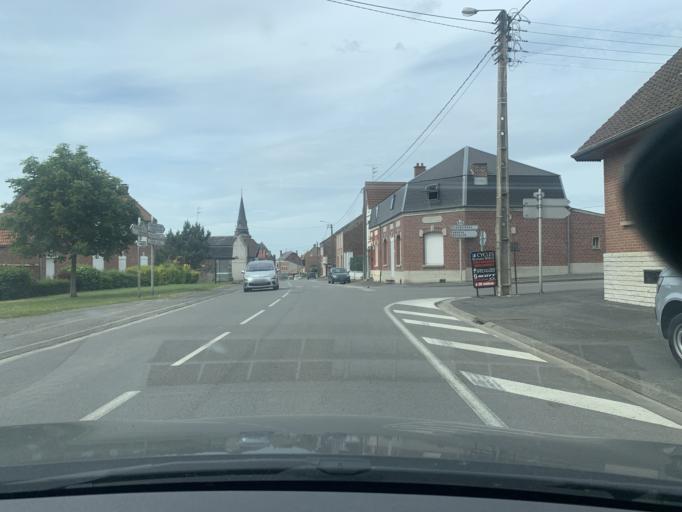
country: FR
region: Nord-Pas-de-Calais
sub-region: Departement du Nord
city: Marcoing
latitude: 50.1242
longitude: 3.1734
